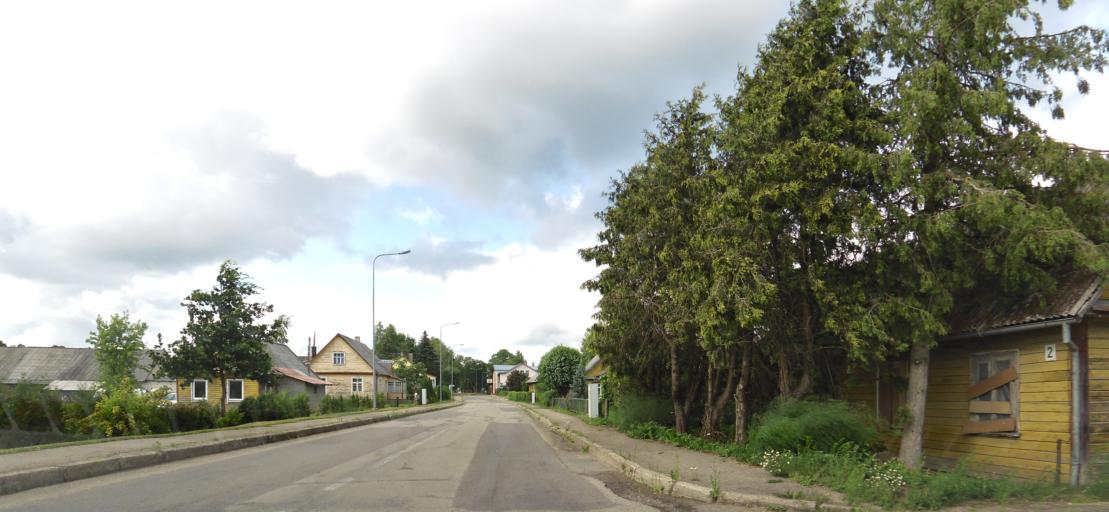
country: LT
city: Obeliai
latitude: 55.8912
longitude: 25.2011
